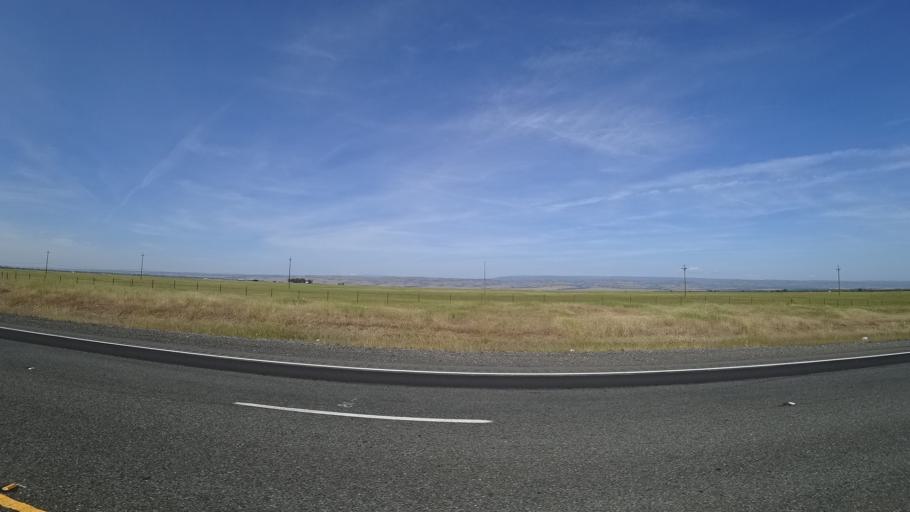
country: US
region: California
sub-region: Tehama County
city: Los Molinos
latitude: 39.9026
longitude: -121.9995
